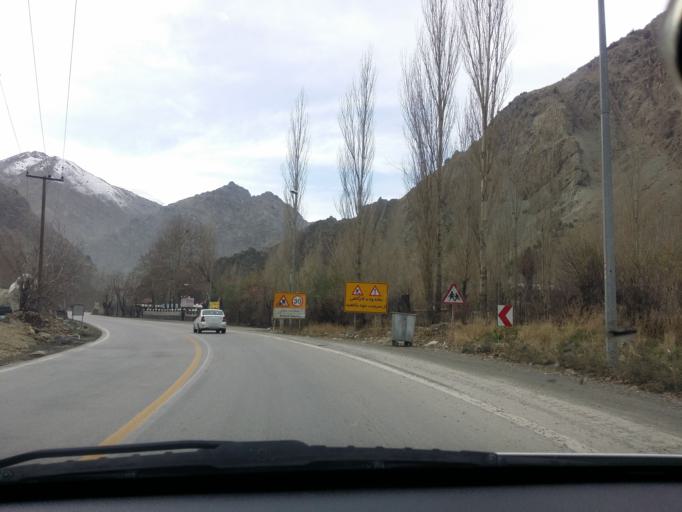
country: IR
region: Tehran
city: Tajrish
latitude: 36.0210
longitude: 51.3012
